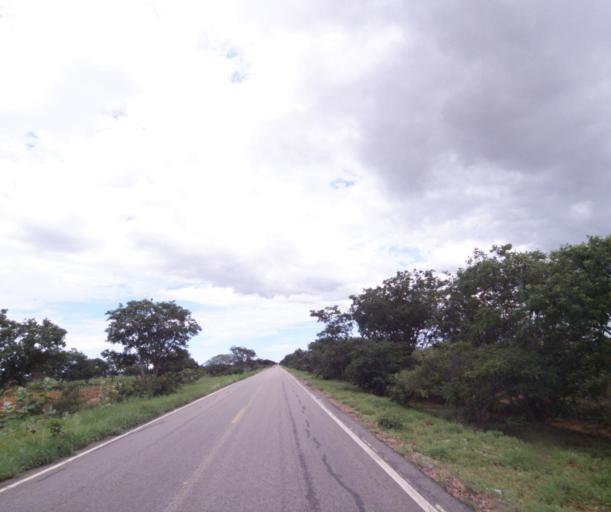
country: BR
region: Bahia
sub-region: Palmas De Monte Alto
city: Palmas de Monte Alto
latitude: -14.2630
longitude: -43.3280
